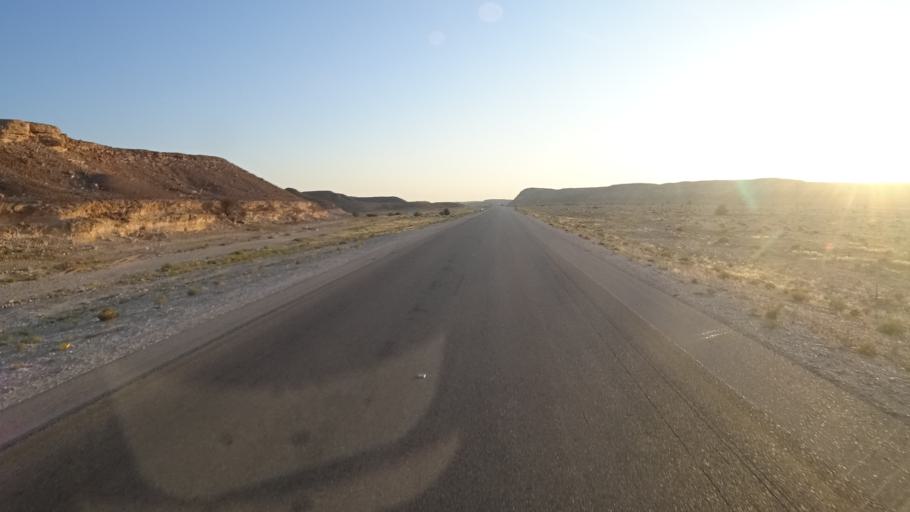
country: OM
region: Zufar
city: Salalah
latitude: 17.5298
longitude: 53.3823
